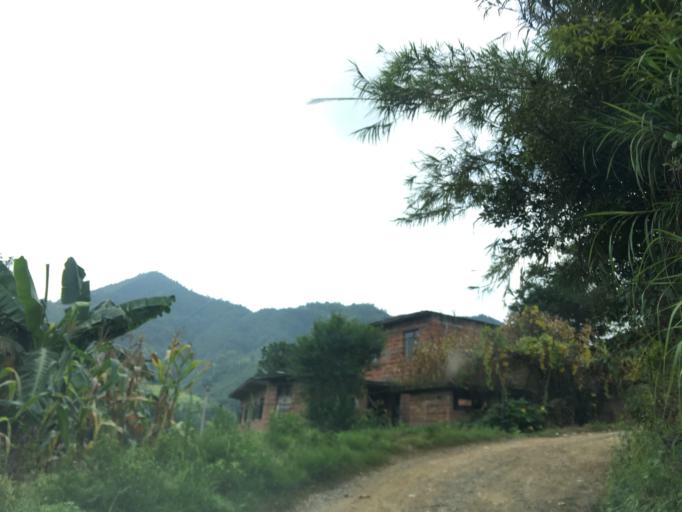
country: CN
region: Guangxi Zhuangzu Zizhiqu
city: Xinzhou
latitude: 24.8878
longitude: 105.8412
